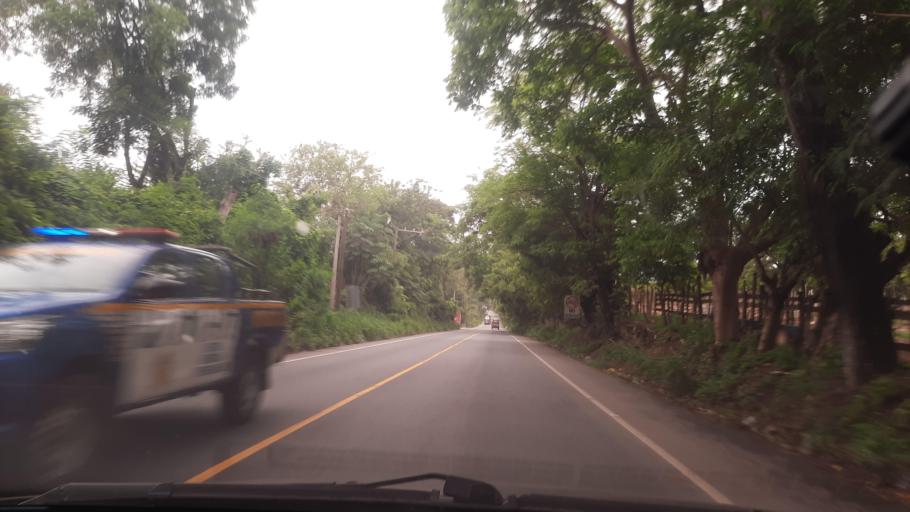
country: GT
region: Zacapa
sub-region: Municipio de Zacapa
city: Gualan
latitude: 15.1707
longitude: -89.3068
